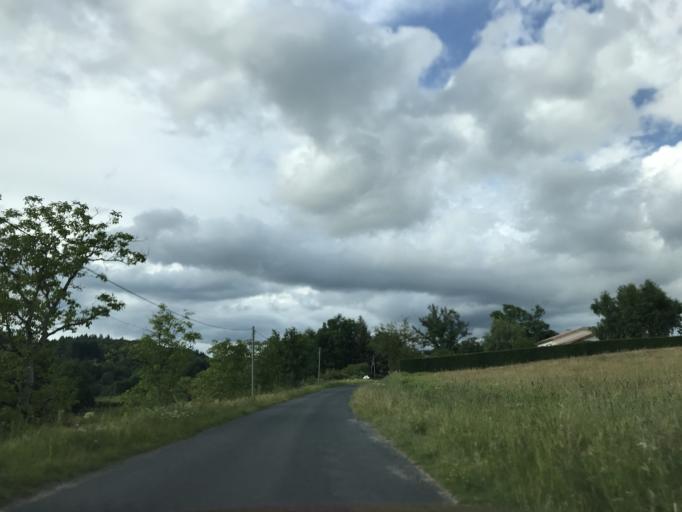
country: FR
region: Auvergne
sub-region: Departement du Puy-de-Dome
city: Celles-sur-Durolle
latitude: 45.8194
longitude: 3.6104
